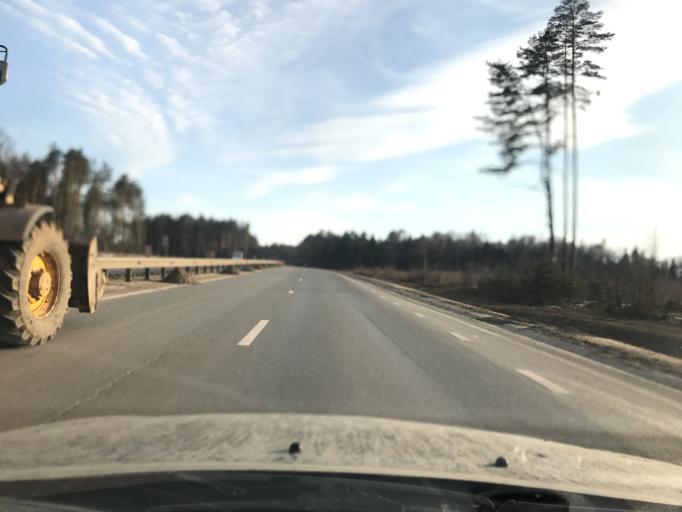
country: RU
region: Kaluga
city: Kaluga
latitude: 54.4182
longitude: 36.2015
